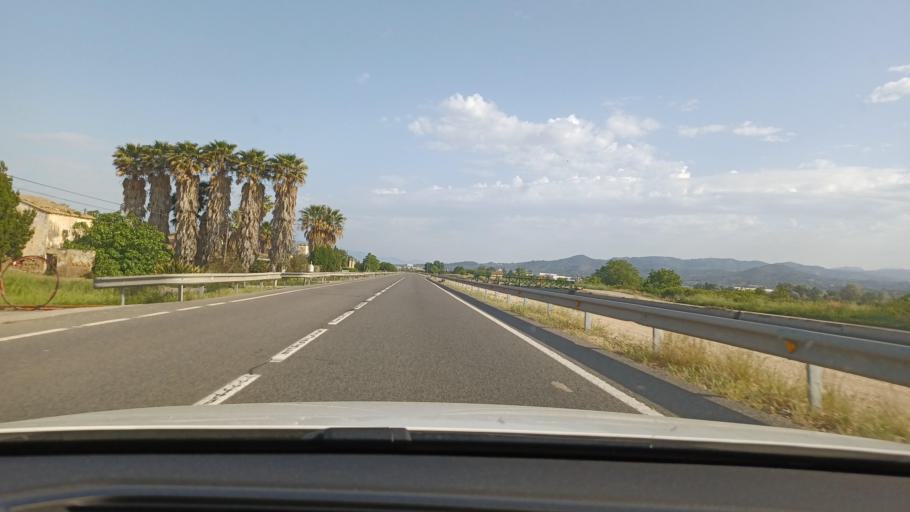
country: ES
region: Catalonia
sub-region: Provincia de Tarragona
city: Amposta
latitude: 40.7356
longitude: 0.5678
